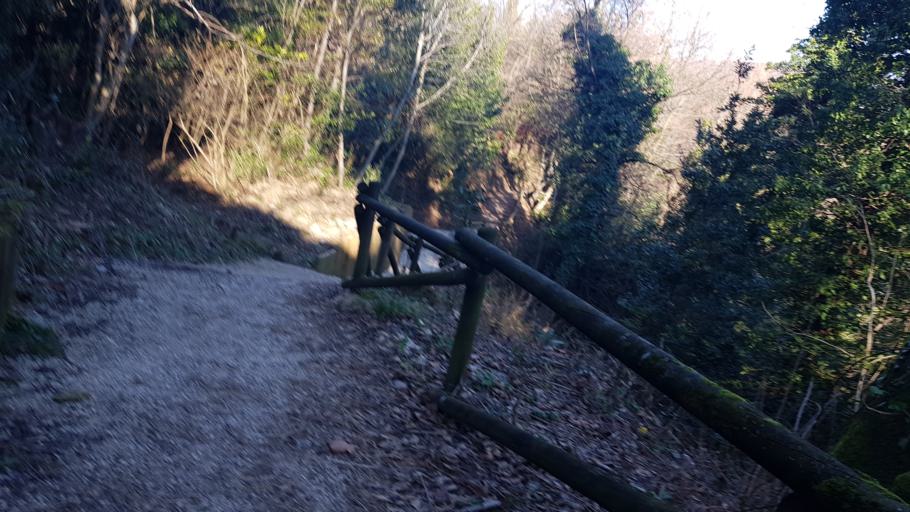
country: IT
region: Friuli Venezia Giulia
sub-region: Provincia di Gorizia
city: Gorizia
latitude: 45.9449
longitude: 13.6280
